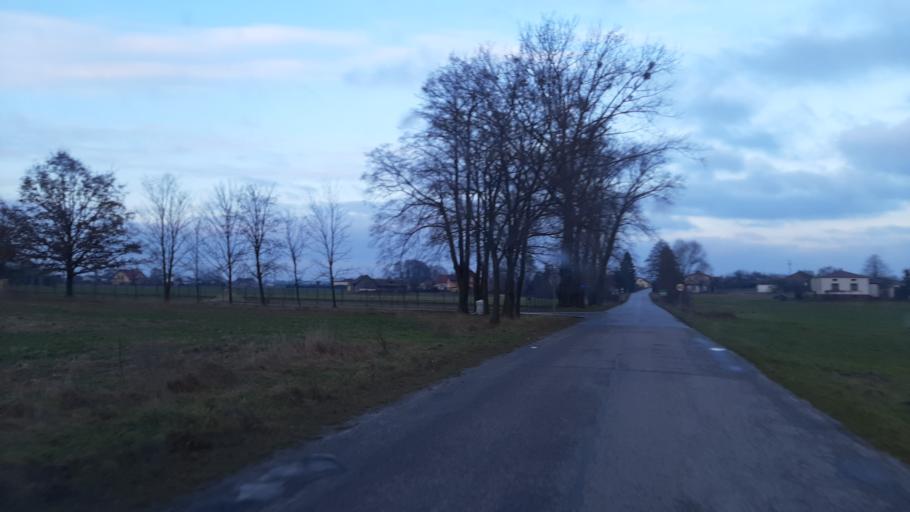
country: PL
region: Lublin Voivodeship
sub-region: Powiat lubartowski
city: Kamionka
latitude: 51.3991
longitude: 22.4114
